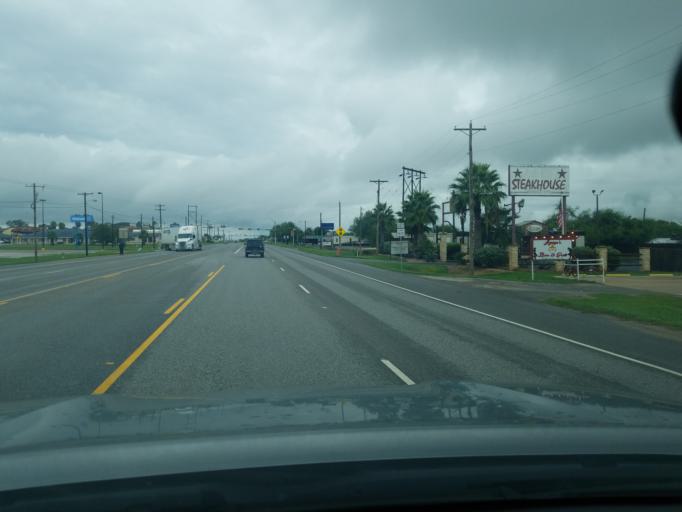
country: US
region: Texas
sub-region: Dimmit County
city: Carrizo Springs
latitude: 28.5408
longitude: -99.8482
